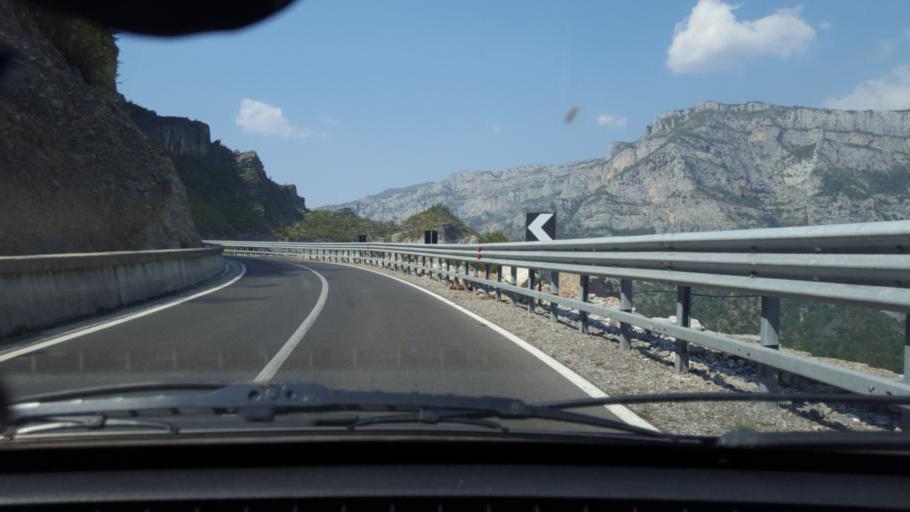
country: AL
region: Shkoder
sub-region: Rrethi i Malesia e Madhe
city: Kastrat
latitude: 42.4148
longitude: 19.5089
